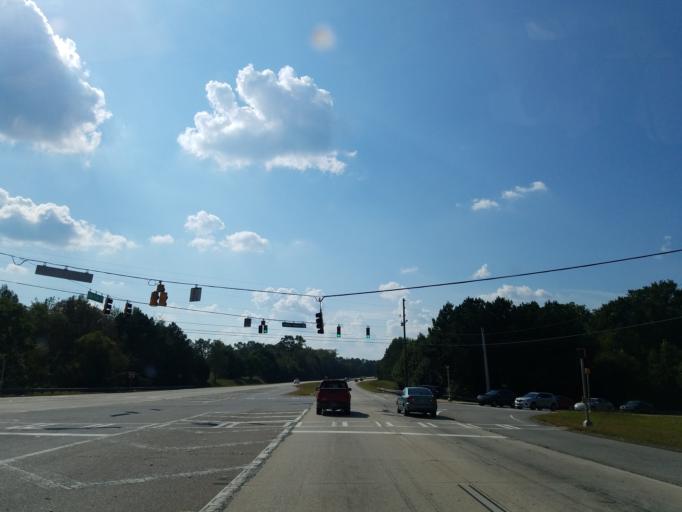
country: US
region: Georgia
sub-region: Oconee County
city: Bogart
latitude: 33.9174
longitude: -83.4816
